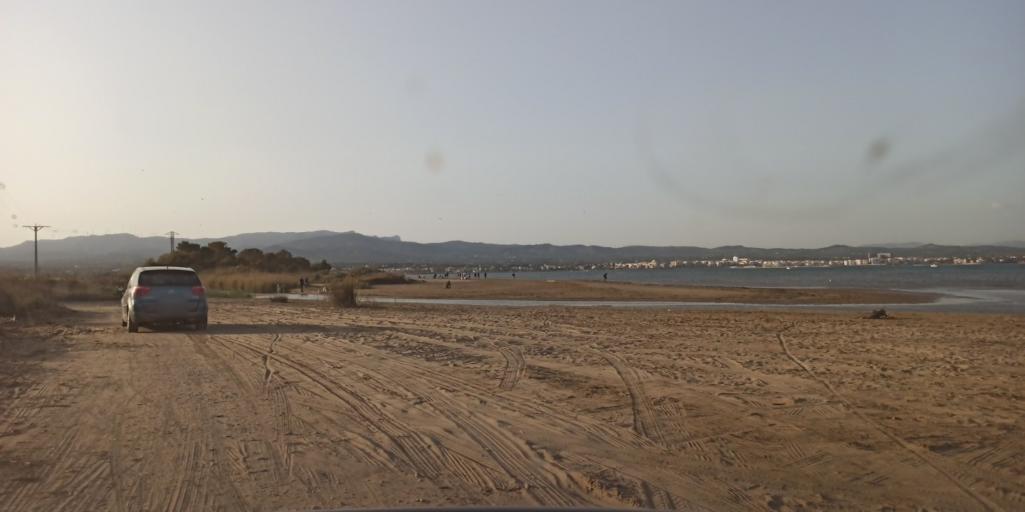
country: ES
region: Catalonia
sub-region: Provincia de Tarragona
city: L'Ampolla
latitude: 40.7854
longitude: 0.7098
